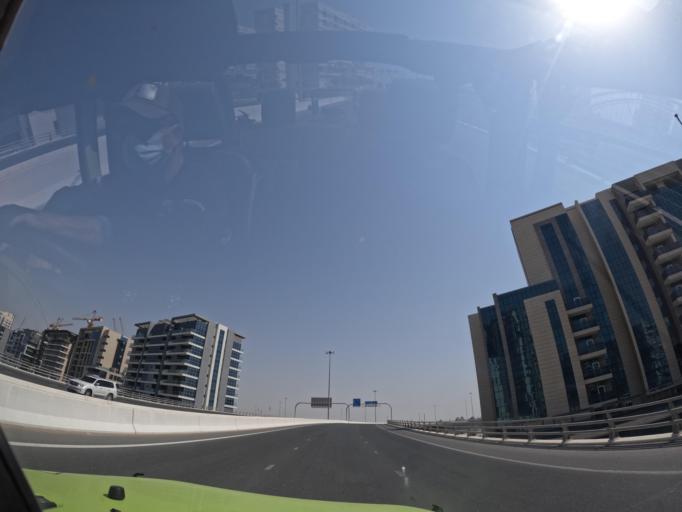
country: AE
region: Abu Dhabi
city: Abu Dhabi
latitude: 24.4433
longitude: 54.5845
